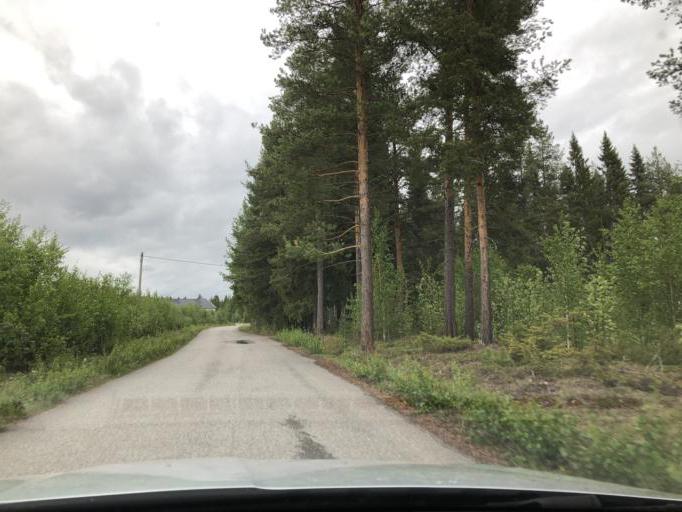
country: SE
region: Norrbotten
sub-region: Pitea Kommun
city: Roknas
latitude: 65.3891
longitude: 21.2696
